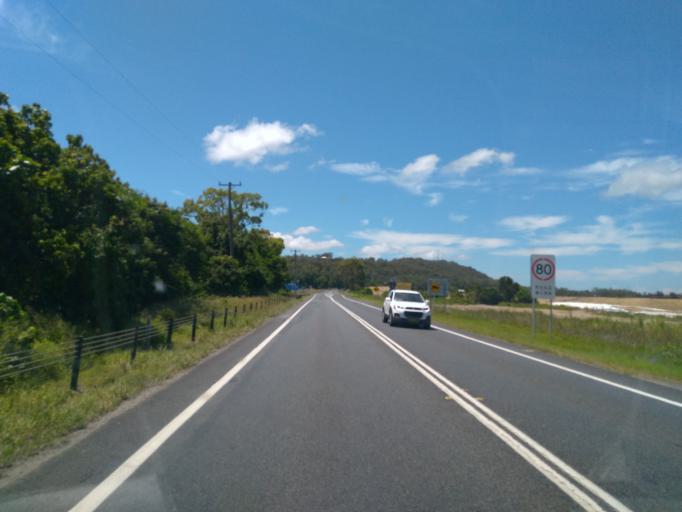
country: AU
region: New South Wales
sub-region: Clarence Valley
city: Maclean
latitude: -29.4757
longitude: 153.2047
